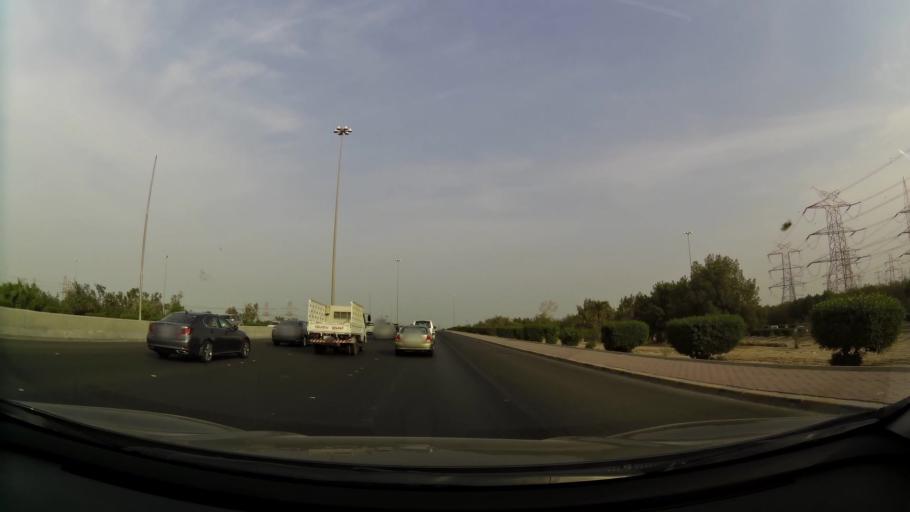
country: KW
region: Mubarak al Kabir
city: Sabah as Salim
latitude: 29.2647
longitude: 48.0385
